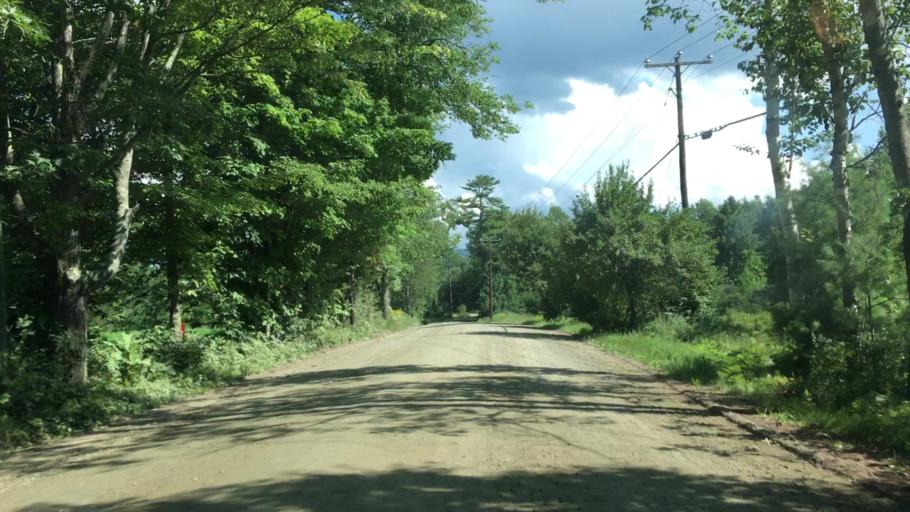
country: US
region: New Hampshire
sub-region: Grafton County
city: North Haverhill
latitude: 44.1316
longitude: -71.9650
